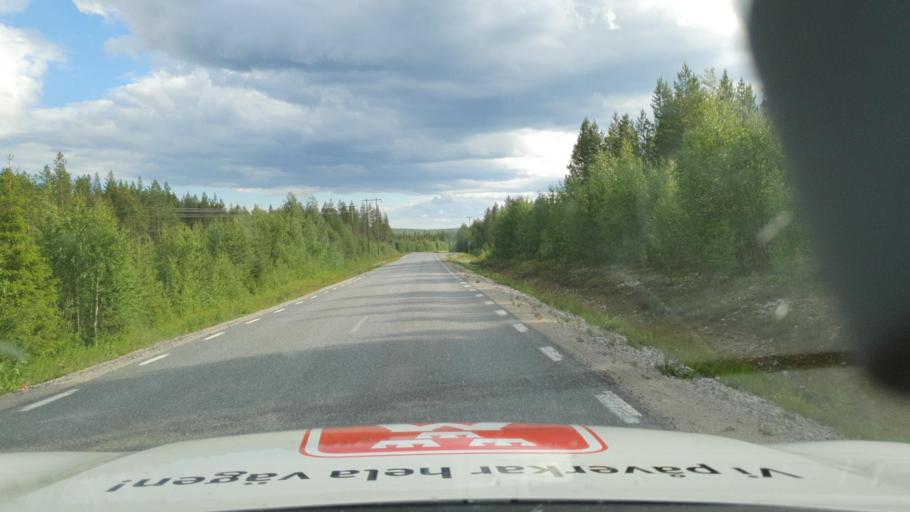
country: SE
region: Vaesterbotten
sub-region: Vindelns Kommun
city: Vindeln
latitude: 64.4282
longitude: 19.7025
